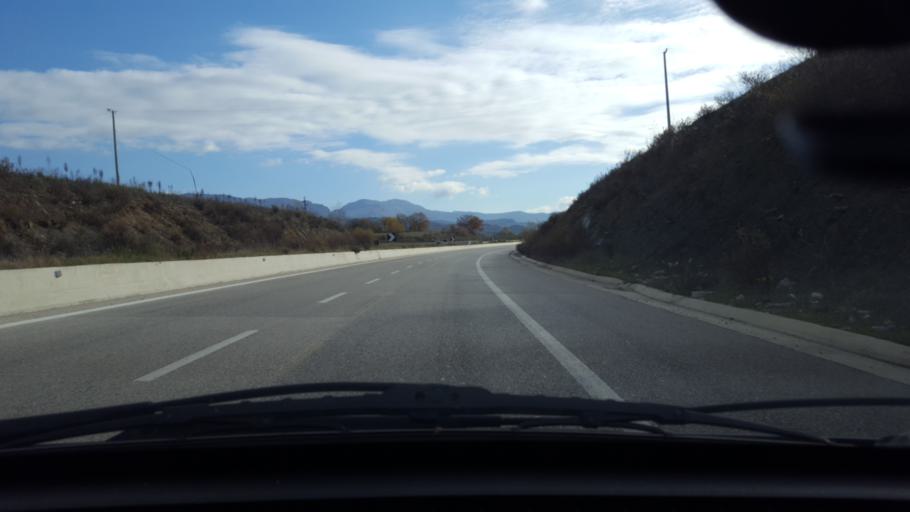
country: AL
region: Tirane
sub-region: Rrethi i Tiranes
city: Berzhite
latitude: 41.2602
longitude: 19.8869
